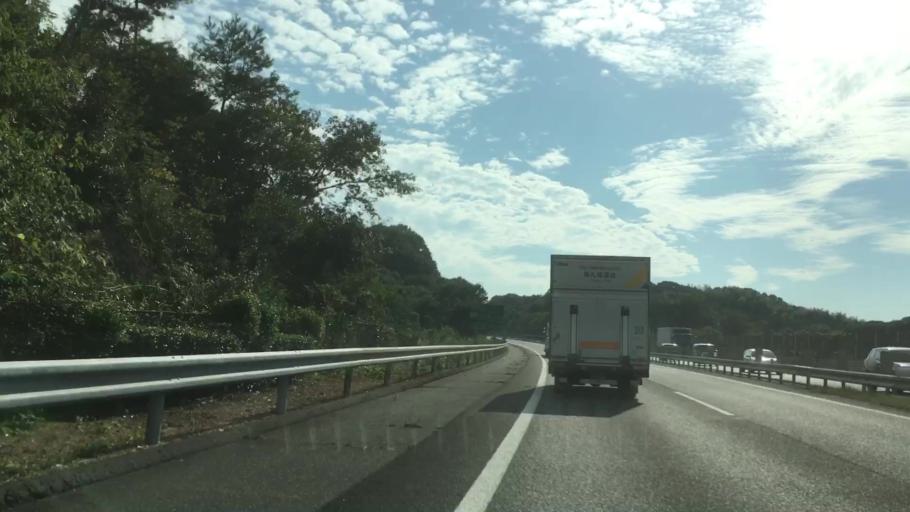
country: JP
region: Yamaguchi
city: Yanai
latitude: 34.0778
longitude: 132.0711
